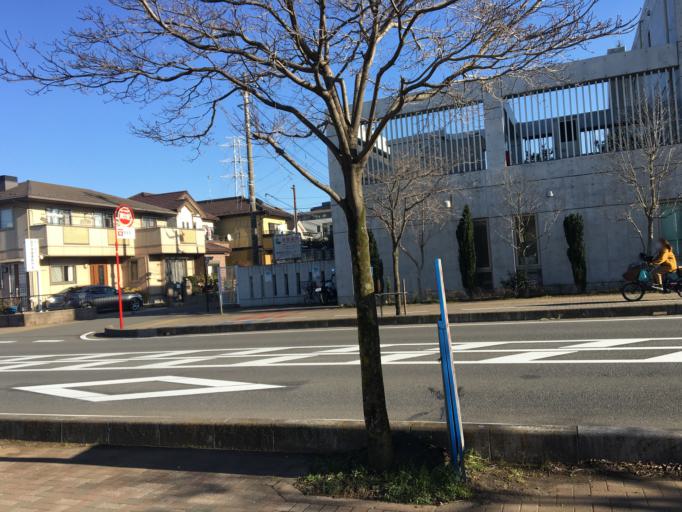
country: JP
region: Saitama
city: Oi
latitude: 35.8423
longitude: 139.5348
